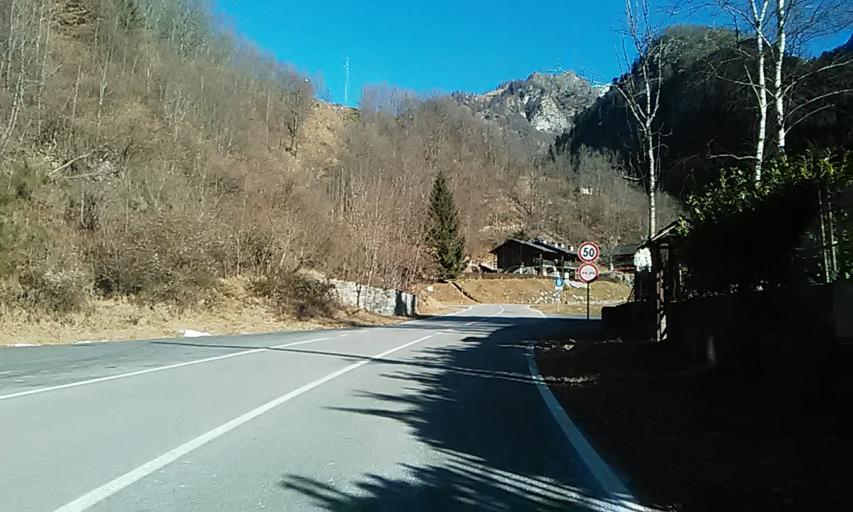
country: IT
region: Piedmont
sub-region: Provincia di Vercelli
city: Rimasco
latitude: 45.8642
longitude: 8.0652
